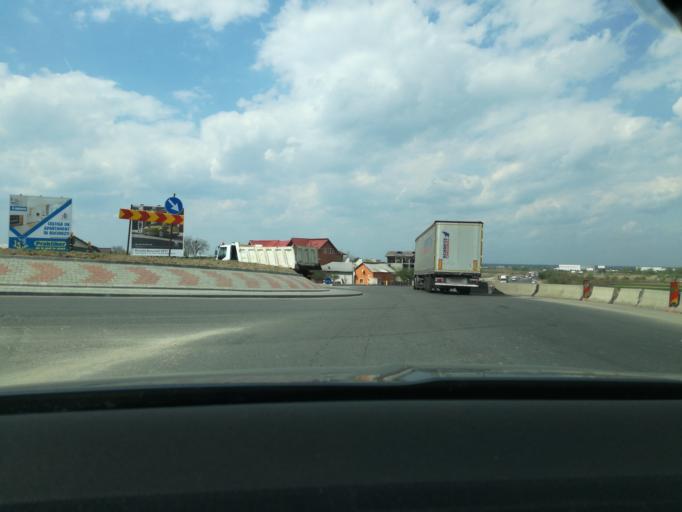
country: RO
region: Ilfov
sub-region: Comuna Dragomiresti-Vale
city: Dragomiresti-Deal
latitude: 44.4554
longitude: 25.9569
